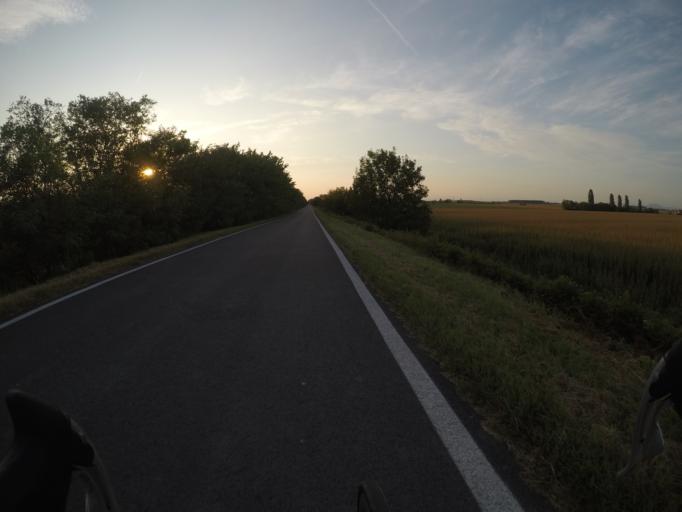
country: IT
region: Veneto
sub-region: Provincia di Rovigo
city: San Bellino
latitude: 44.9982
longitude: 11.5862
